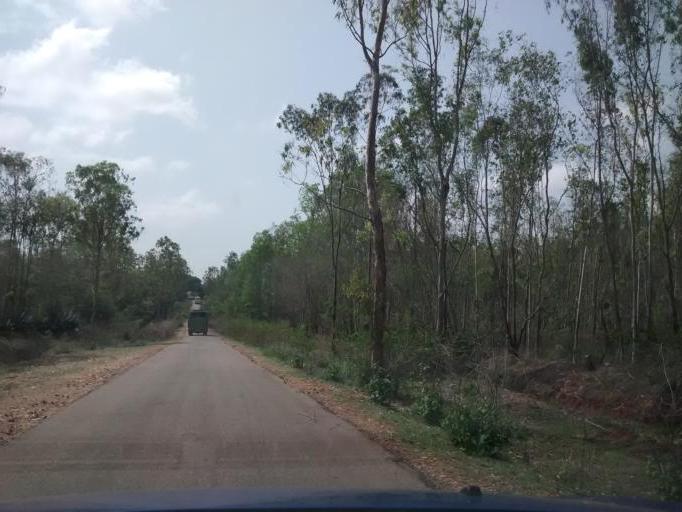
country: IN
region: Karnataka
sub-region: Hassan
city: Arkalgud
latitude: 12.7050
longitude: 76.1517
